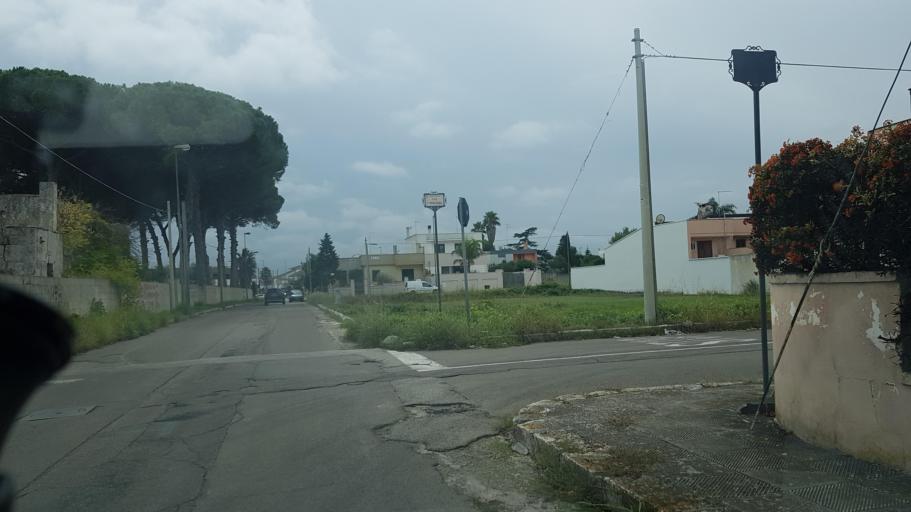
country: IT
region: Apulia
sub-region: Provincia di Brindisi
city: Cellino San Marco
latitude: 40.4758
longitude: 17.9712
